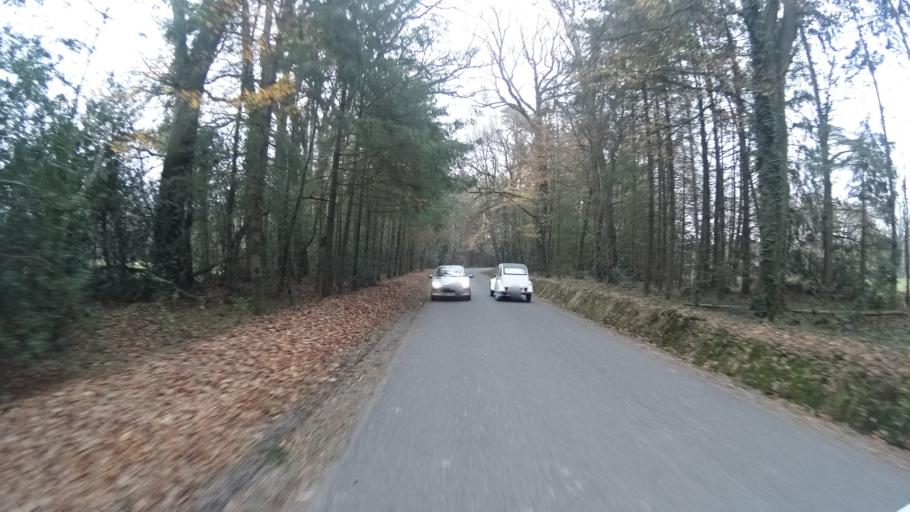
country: FR
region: Brittany
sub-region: Departement d'Ille-et-Vilaine
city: Bains-sur-Oust
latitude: 47.7069
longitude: -2.0509
